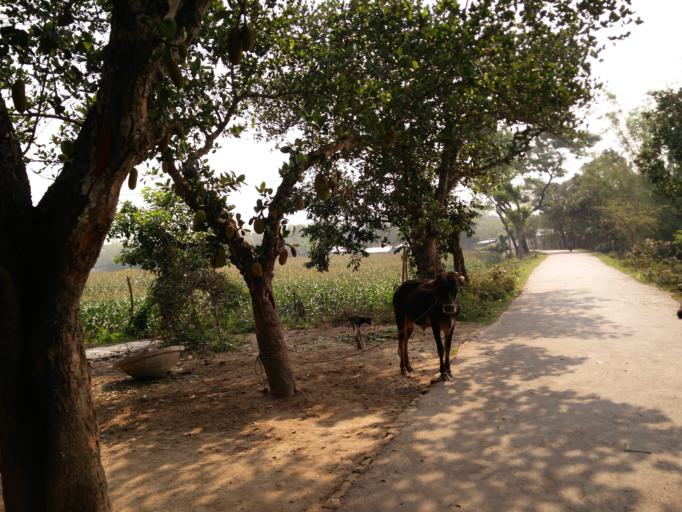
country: BD
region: Dhaka
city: Muktagacha
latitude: 24.9047
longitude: 90.1892
